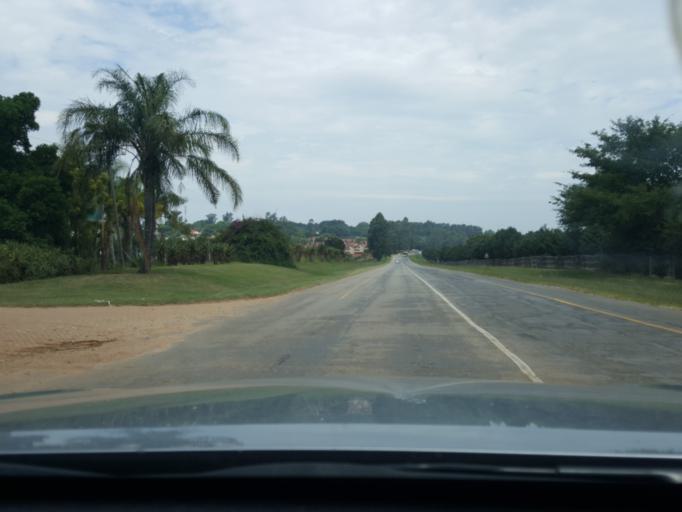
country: ZA
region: Mpumalanga
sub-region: Ehlanzeni District
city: White River
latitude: -25.3283
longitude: 30.9916
